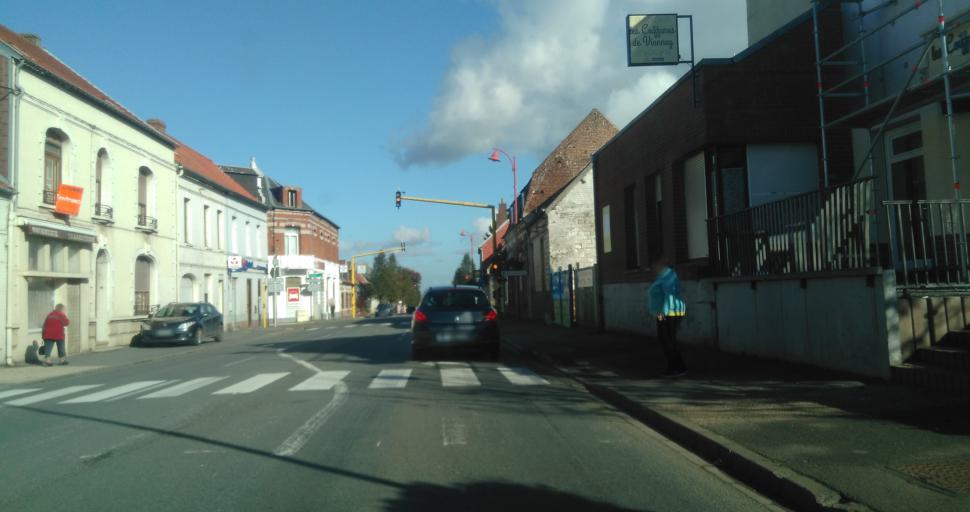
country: FR
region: Nord-Pas-de-Calais
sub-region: Departement du Pas-de-Calais
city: Beaumetz-les-Loges
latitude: 50.2410
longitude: 2.6582
